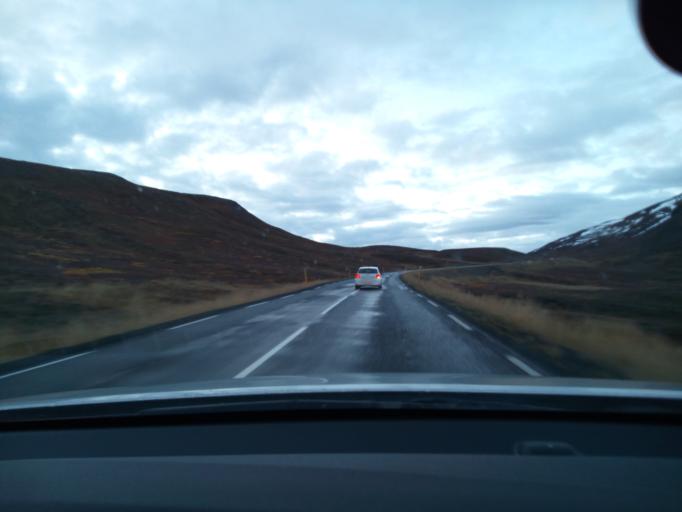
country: IS
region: Northeast
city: Akureyri
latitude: 65.7973
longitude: -17.9443
